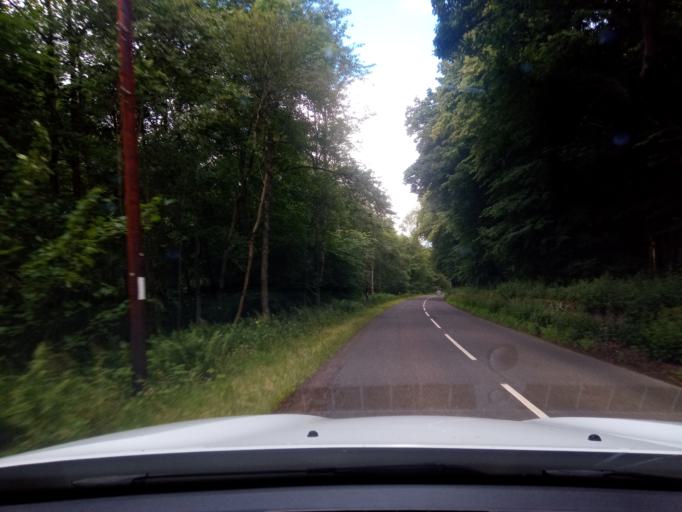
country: GB
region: Scotland
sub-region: The Scottish Borders
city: Selkirk
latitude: 55.5405
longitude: -2.8971
